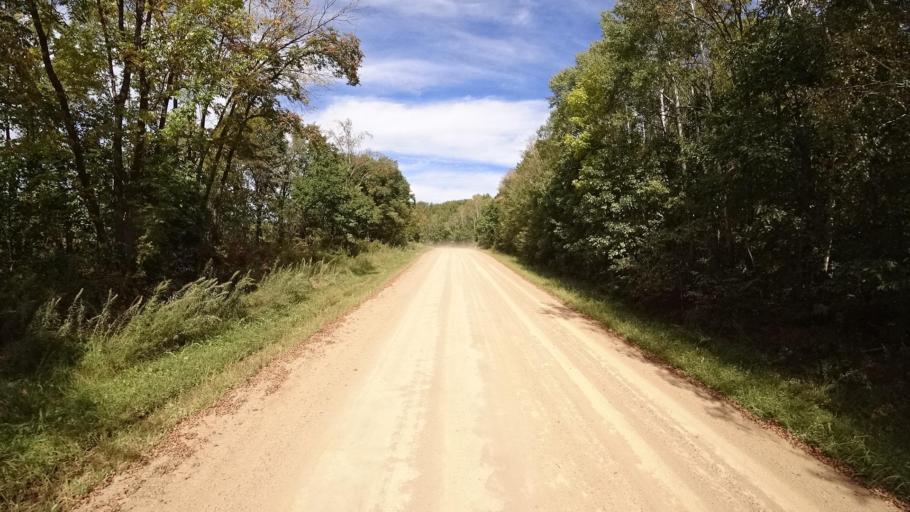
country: RU
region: Primorskiy
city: Yakovlevka
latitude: 44.6286
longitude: 133.6012
